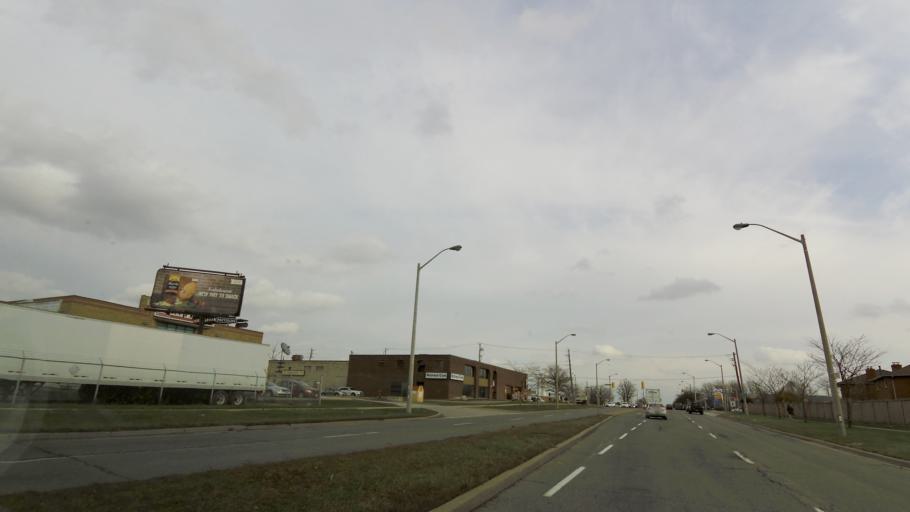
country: CA
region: Ontario
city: Etobicoke
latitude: 43.7352
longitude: -79.6197
